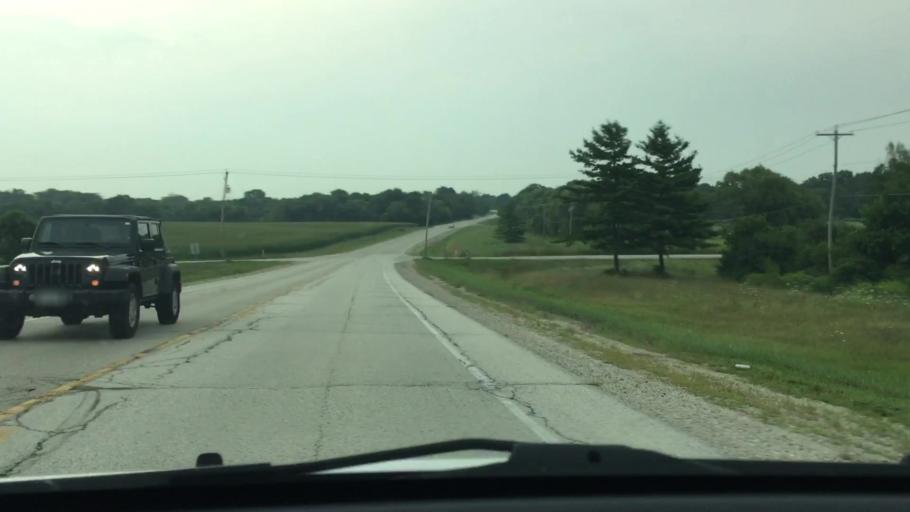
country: US
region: Wisconsin
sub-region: Waukesha County
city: New Berlin
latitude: 42.9936
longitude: -88.1684
